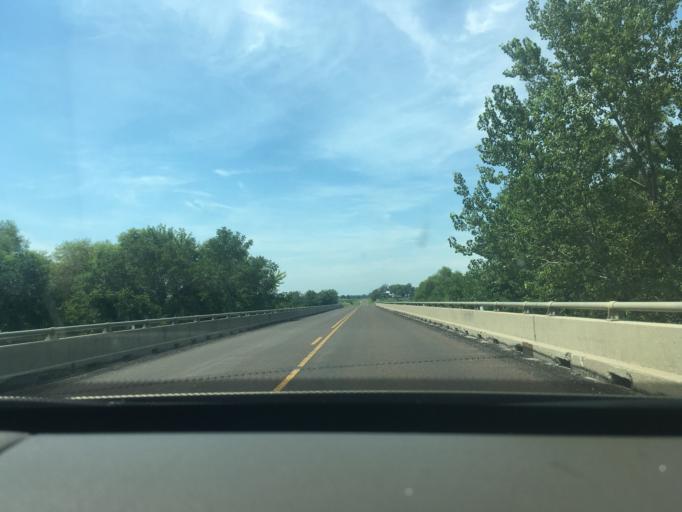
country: US
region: Missouri
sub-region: Gentry County
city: Stanberry
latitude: 40.1704
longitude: -94.7459
